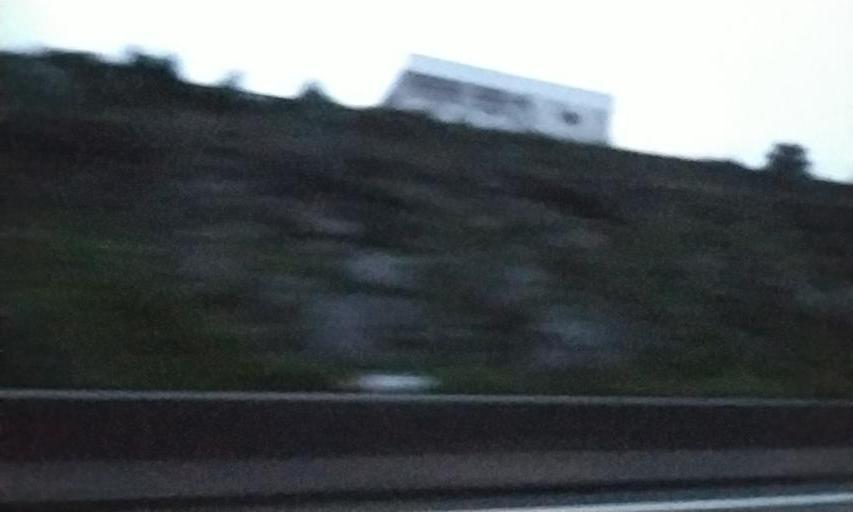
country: PT
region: Braga
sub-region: Braga
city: Braga
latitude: 41.5243
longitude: -8.4460
